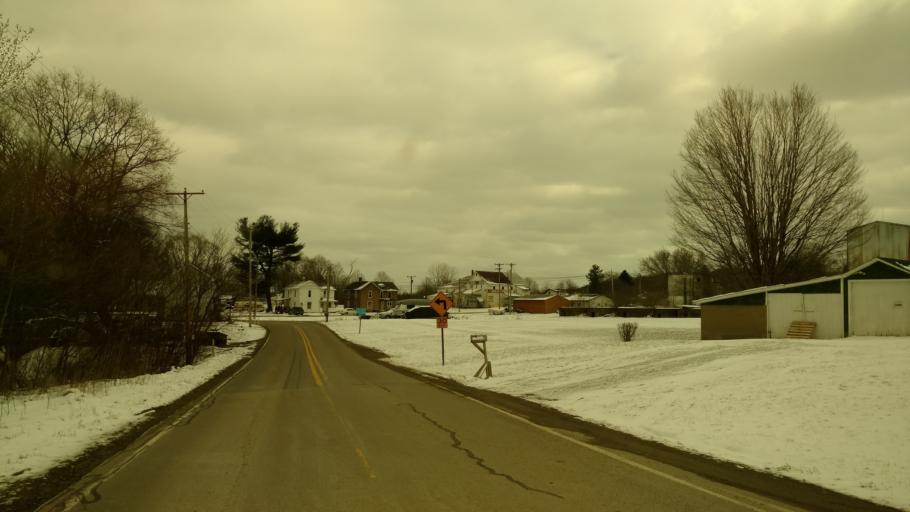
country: US
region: Pennsylvania
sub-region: Mercer County
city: Mercer
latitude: 41.3245
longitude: -80.2597
